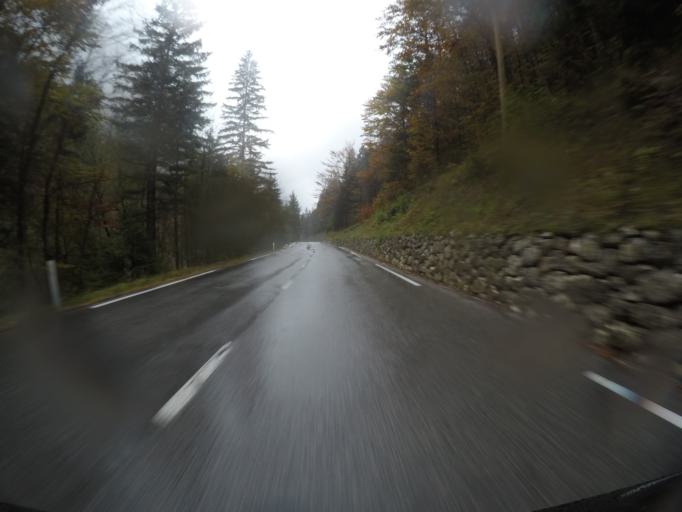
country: SI
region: Kranjska Gora
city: Kranjska Gora
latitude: 46.3527
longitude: 13.6948
